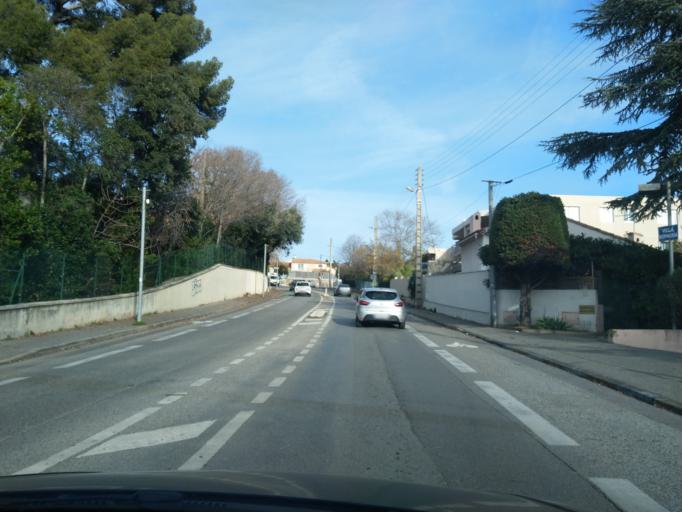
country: FR
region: Provence-Alpes-Cote d'Azur
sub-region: Departement des Bouches-du-Rhone
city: Marseille 12
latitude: 43.3022
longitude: 5.4377
